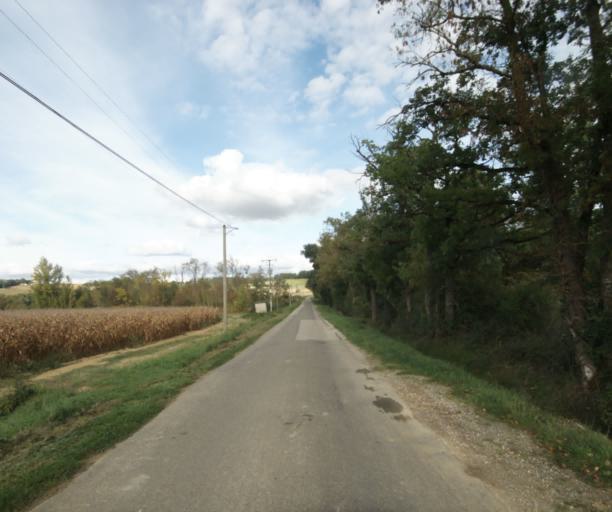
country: FR
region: Midi-Pyrenees
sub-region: Departement du Gers
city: Gondrin
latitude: 43.8705
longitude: 0.2167
